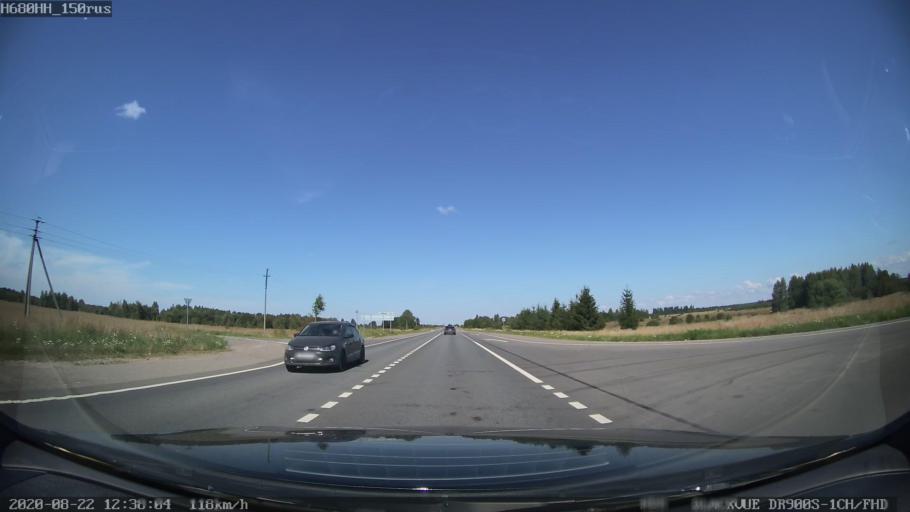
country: RU
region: Tverskaya
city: Rameshki
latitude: 57.3077
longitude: 36.0886
